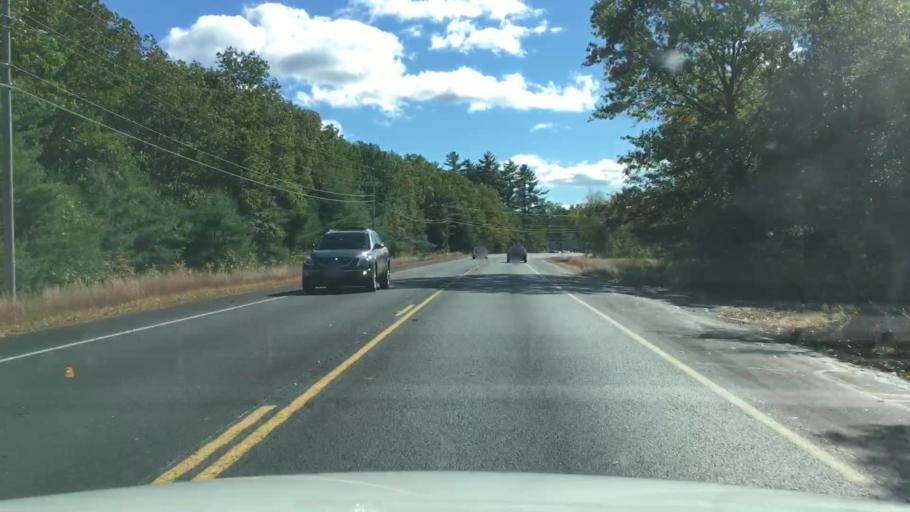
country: US
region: Maine
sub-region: York County
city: Alfred
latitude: 43.4630
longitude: -70.7197
